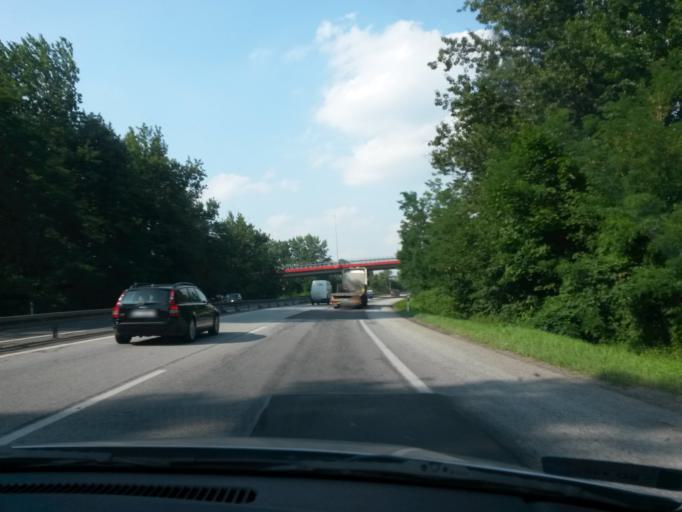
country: PL
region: Silesian Voivodeship
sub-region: Myslowice
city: Myslowice
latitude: 50.2412
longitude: 19.1702
